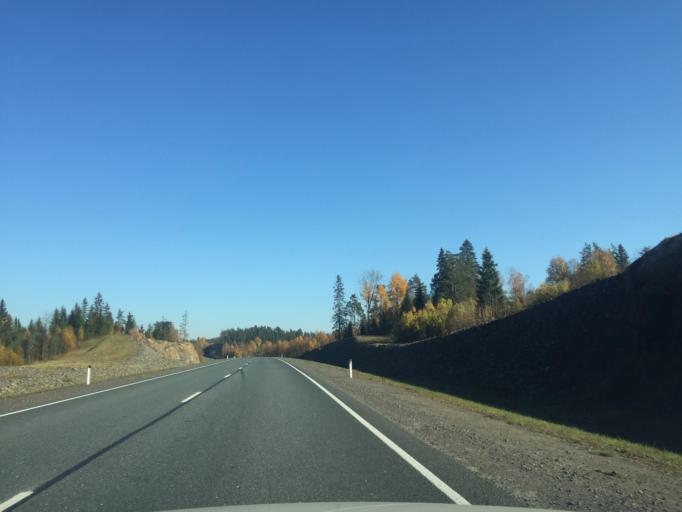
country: RU
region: Leningrad
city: Kuznechnoye
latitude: 61.3440
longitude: 29.8714
